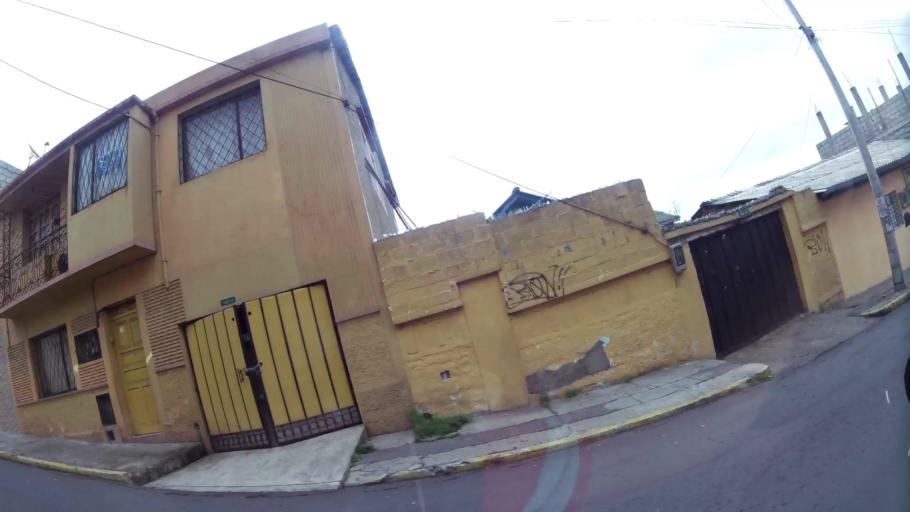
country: EC
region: Pichincha
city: Quito
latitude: -0.2114
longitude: -78.5116
